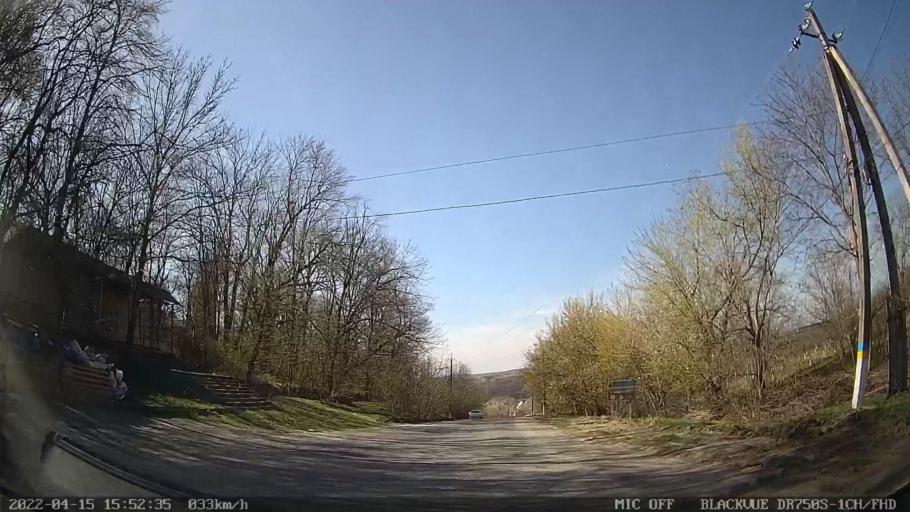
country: MD
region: Raionul Ocnita
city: Otaci
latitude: 48.3952
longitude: 27.8918
